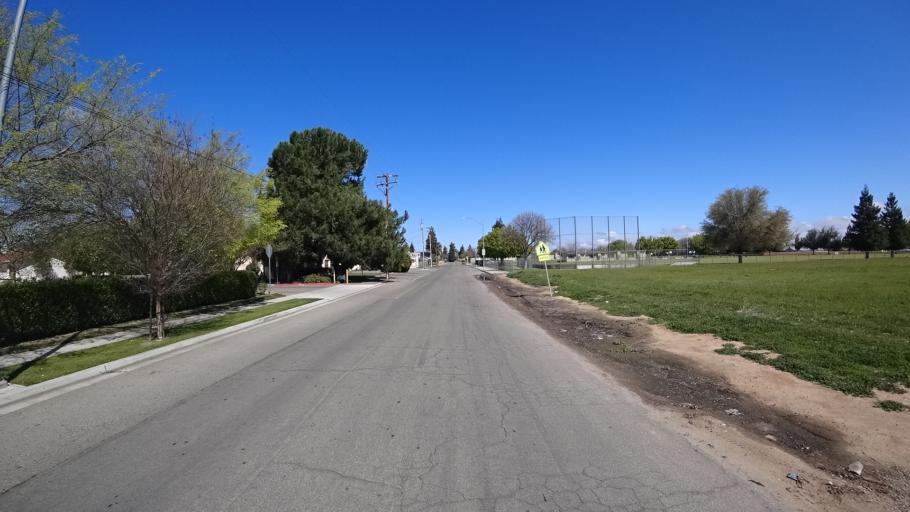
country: US
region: California
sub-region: Fresno County
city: West Park
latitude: 36.7868
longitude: -119.8759
